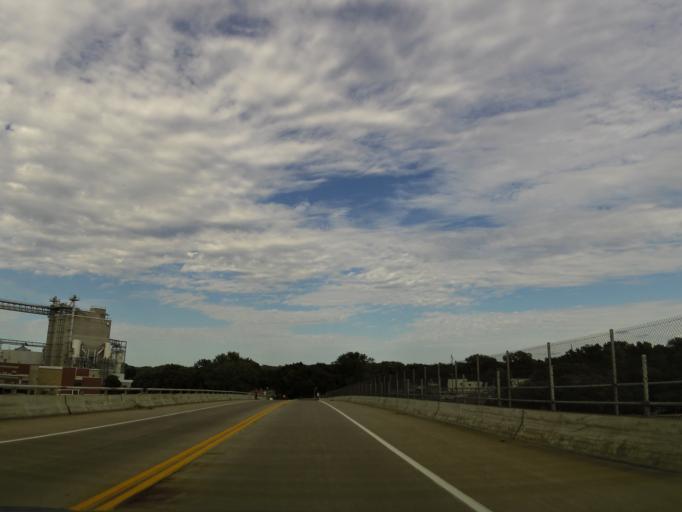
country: US
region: Minnesota
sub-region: Anoka County
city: Columbia Heights
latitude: 45.0460
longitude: -93.2724
